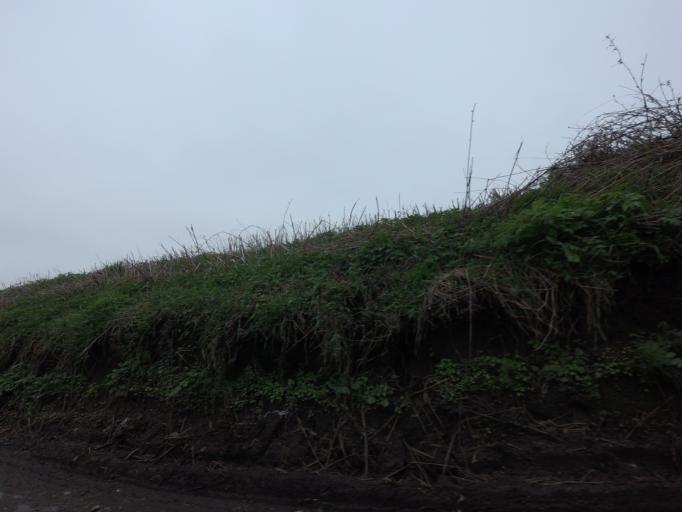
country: GB
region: England
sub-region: Kent
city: Swanley
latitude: 51.3662
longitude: 0.1537
